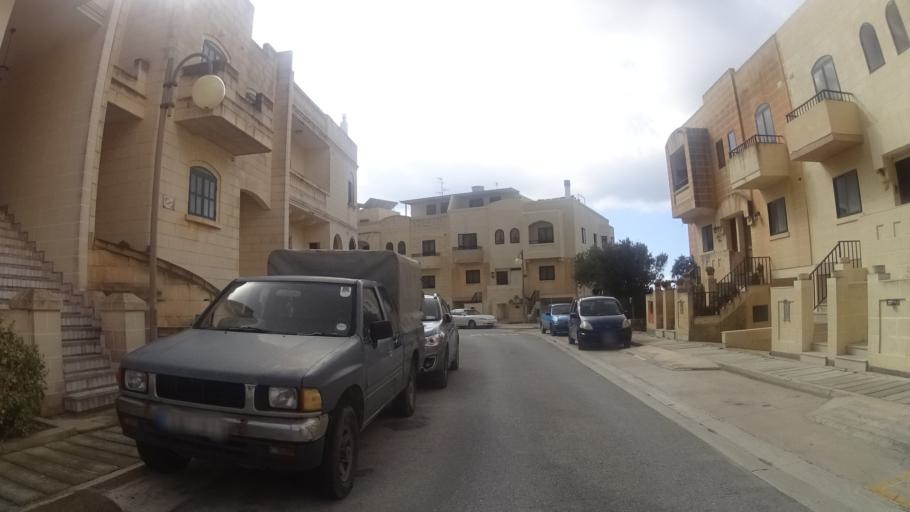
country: MT
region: L-Imtarfa
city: Imtarfa
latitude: 35.8900
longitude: 14.3925
